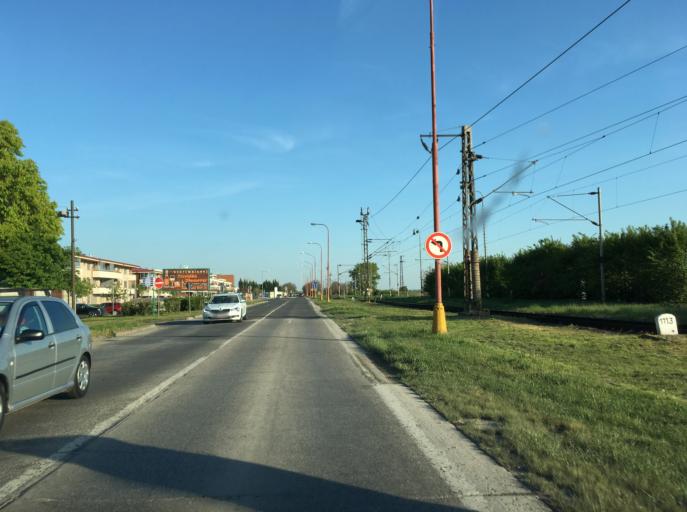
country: AT
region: Burgenland
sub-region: Politischer Bezirk Neusiedl am See
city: Deutsch Jahrndorf
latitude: 48.0445
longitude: 17.1544
